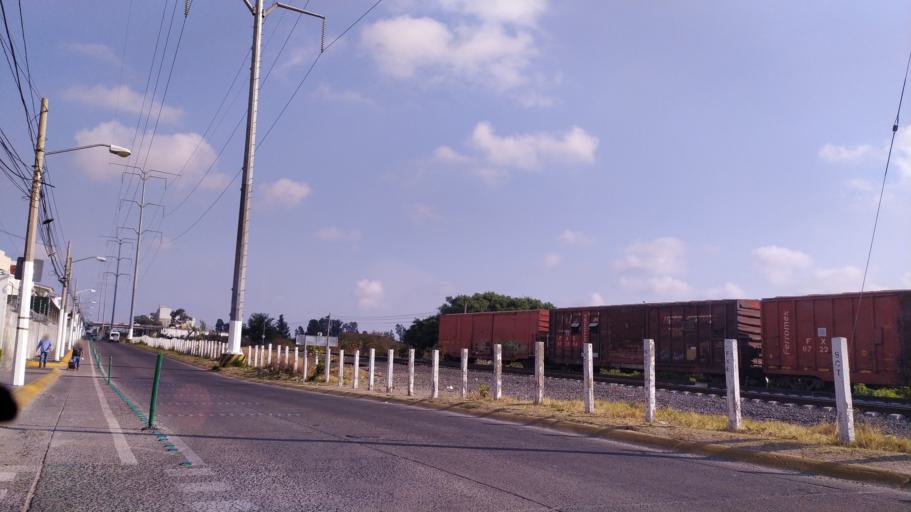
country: MX
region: Jalisco
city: Zapopan2
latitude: 20.6984
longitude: -103.4515
